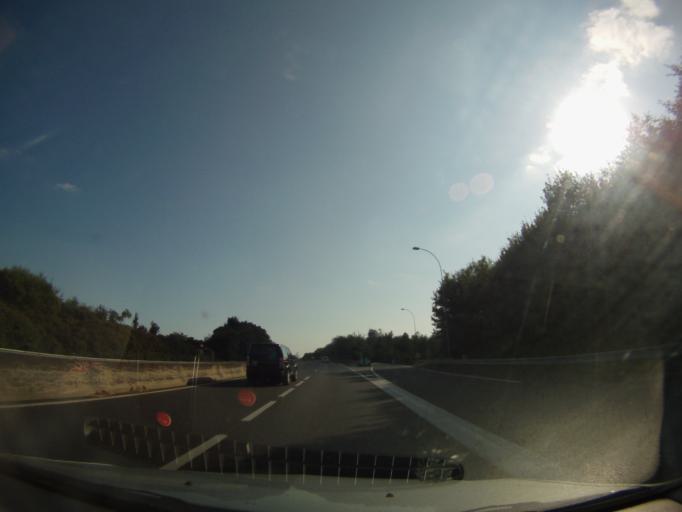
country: FR
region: Pays de la Loire
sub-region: Departement de la Loire-Atlantique
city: Carquefou
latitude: 47.2868
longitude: -1.5069
